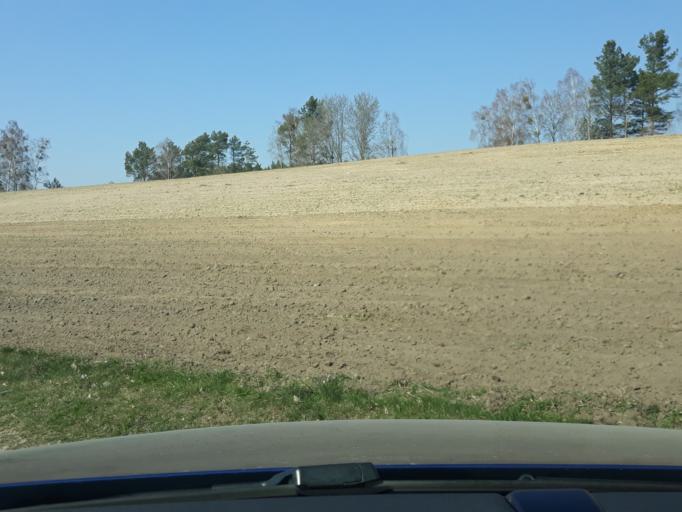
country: PL
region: Pomeranian Voivodeship
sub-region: Powiat bytowski
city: Lipnica
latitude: 53.8600
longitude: 17.4381
